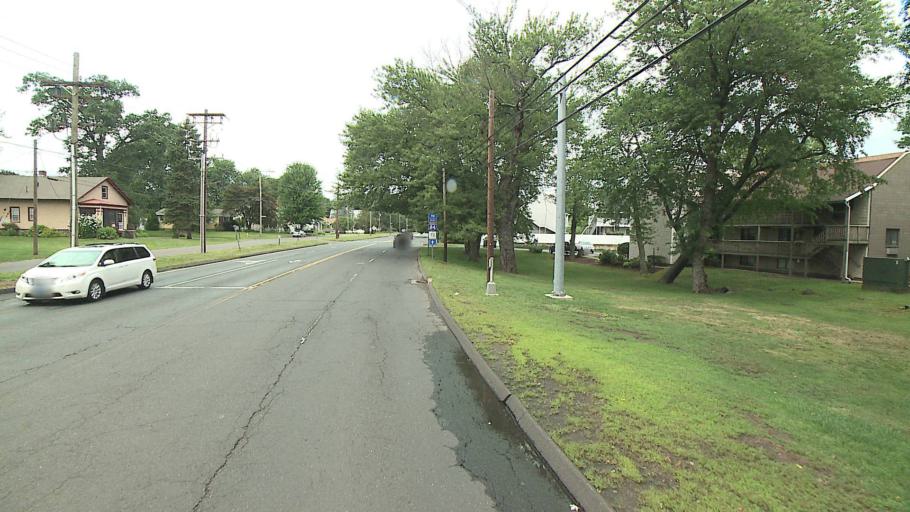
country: US
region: Connecticut
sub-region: Hartford County
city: Plainville
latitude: 41.6688
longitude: -72.8466
